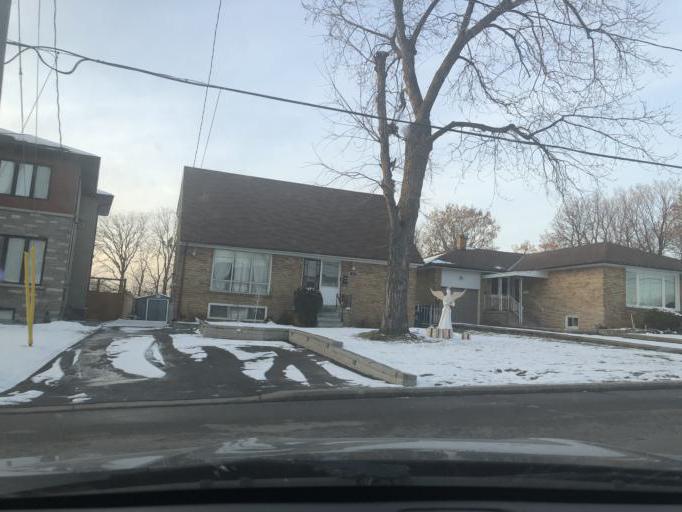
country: CA
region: Ontario
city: Toronto
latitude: 43.7074
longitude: -79.4907
